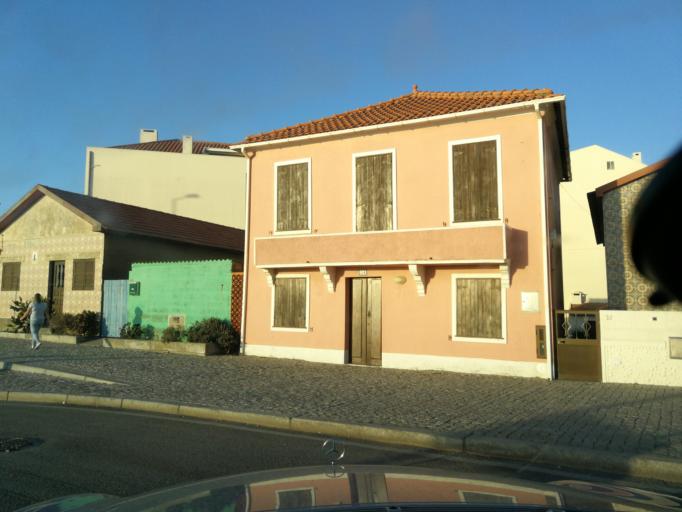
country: PT
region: Aveiro
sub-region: Murtosa
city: Murtosa
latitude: 40.7599
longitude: -8.7132
